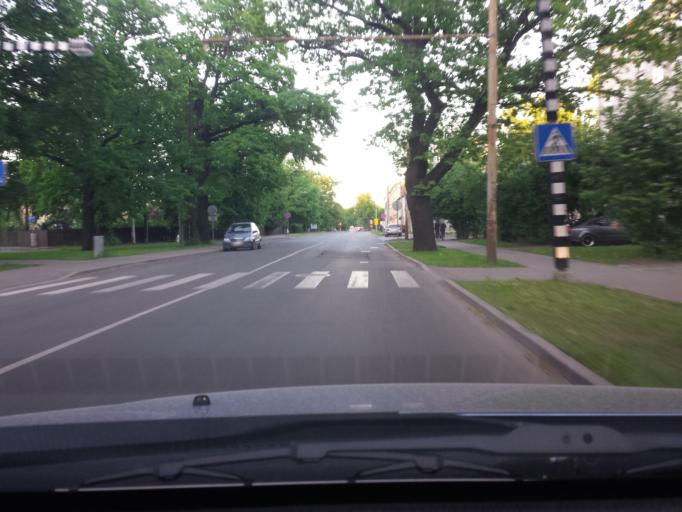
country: LV
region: Riga
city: Jaunciems
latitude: 56.9713
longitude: 24.1744
